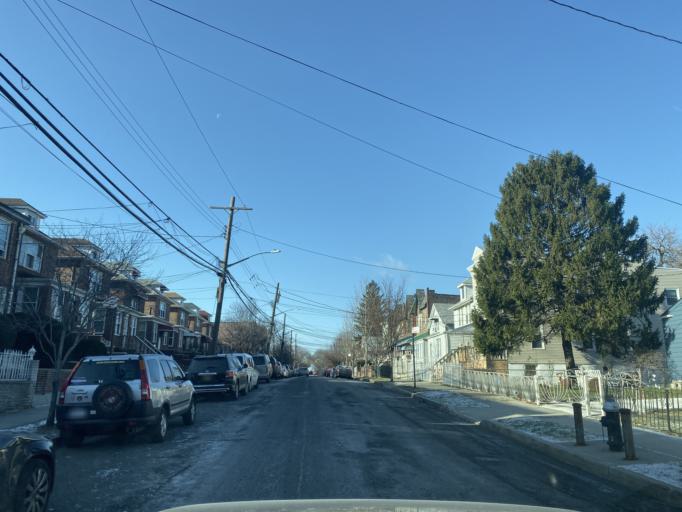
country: US
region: New York
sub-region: Bronx
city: The Bronx
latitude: 40.8258
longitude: -73.8469
